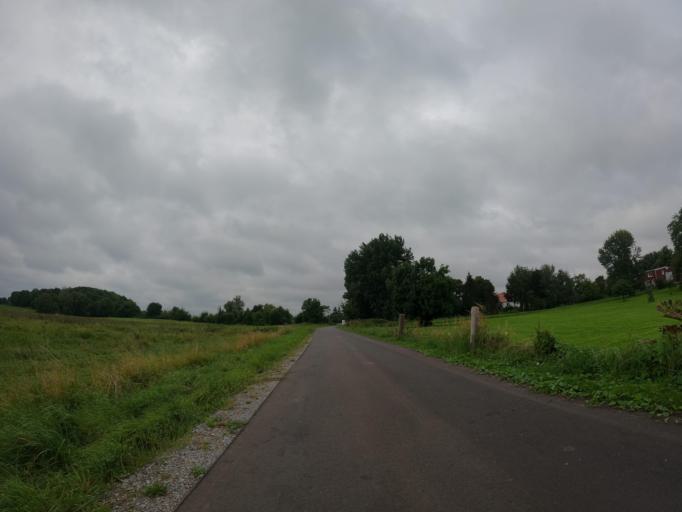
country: DE
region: Mecklenburg-Vorpommern
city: Rambin
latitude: 54.3000
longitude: 13.2094
